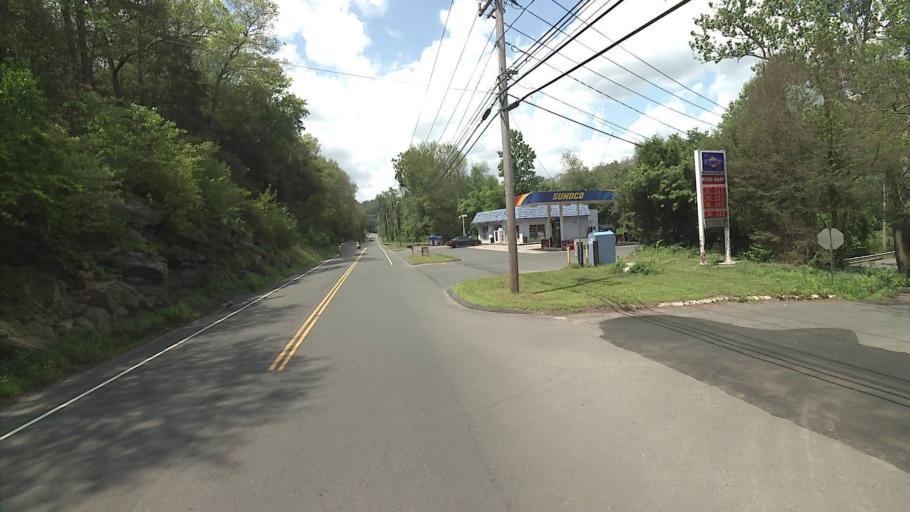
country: US
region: Connecticut
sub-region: Middlesex County
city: Higganum
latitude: 41.5036
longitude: -72.5735
